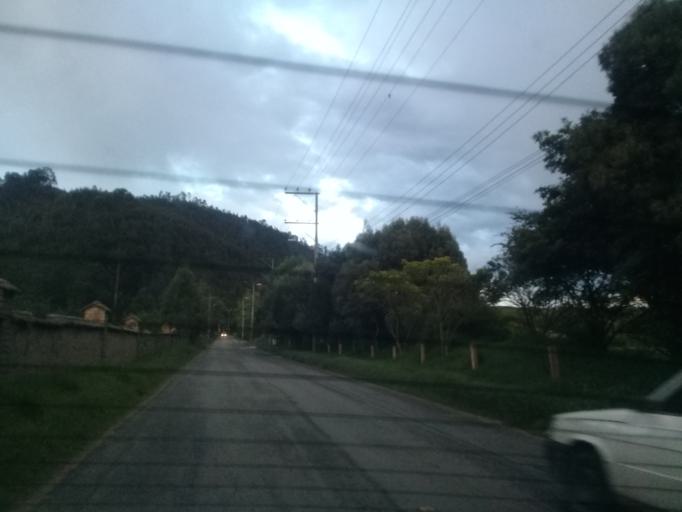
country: CO
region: Cundinamarca
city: Tabio
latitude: 4.9259
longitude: -74.0705
